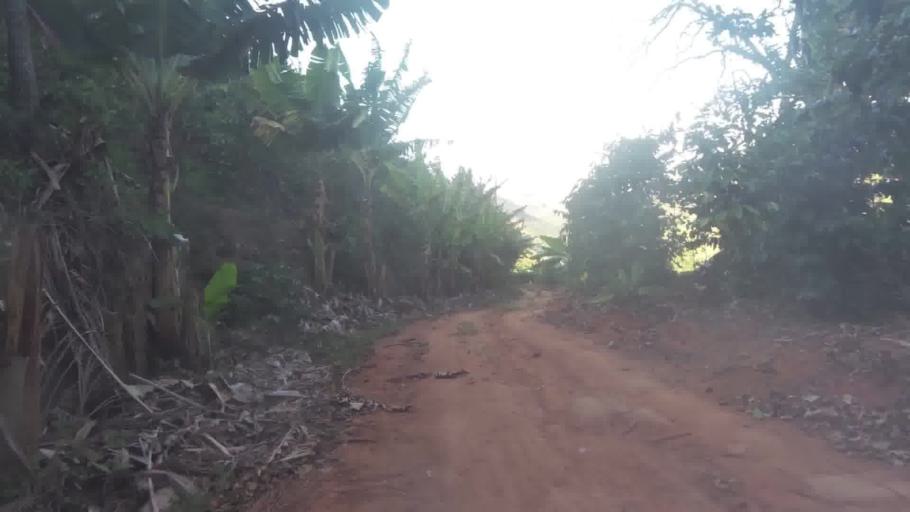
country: BR
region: Espirito Santo
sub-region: Iconha
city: Iconha
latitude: -20.7526
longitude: -40.8080
